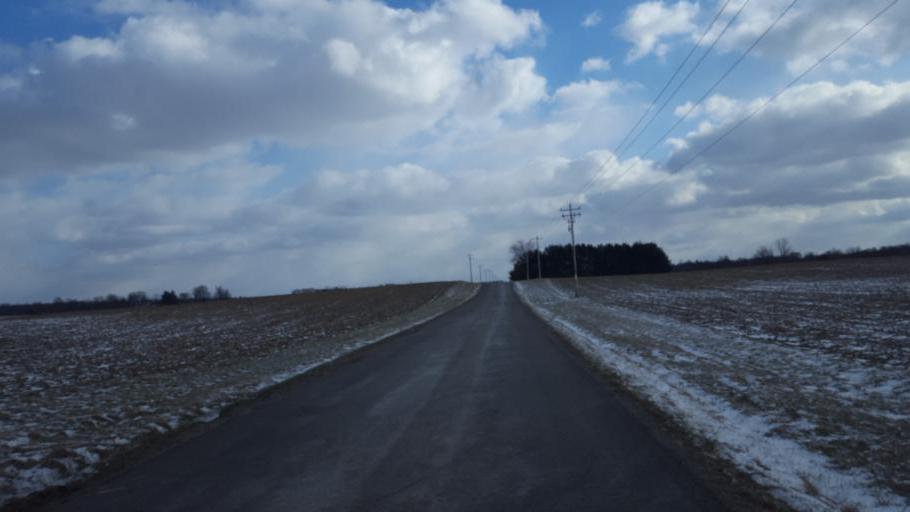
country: US
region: Ohio
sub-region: Crawford County
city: Galion
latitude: 40.6891
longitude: -82.7179
